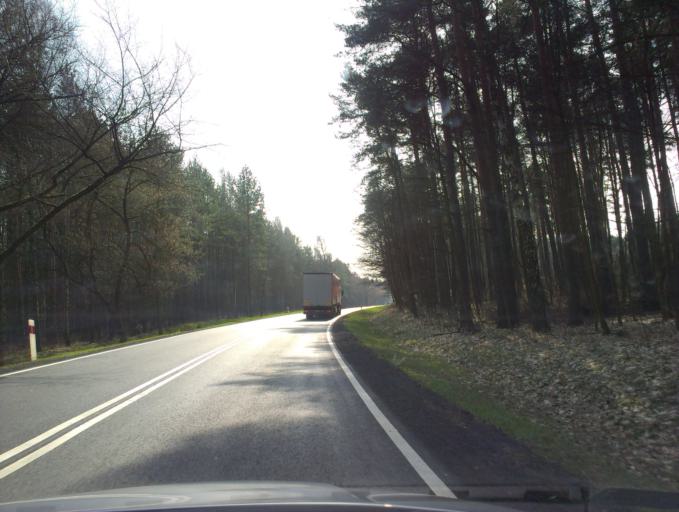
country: PL
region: Greater Poland Voivodeship
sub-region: Powiat zlotowski
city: Okonek
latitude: 53.4991
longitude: 16.8558
